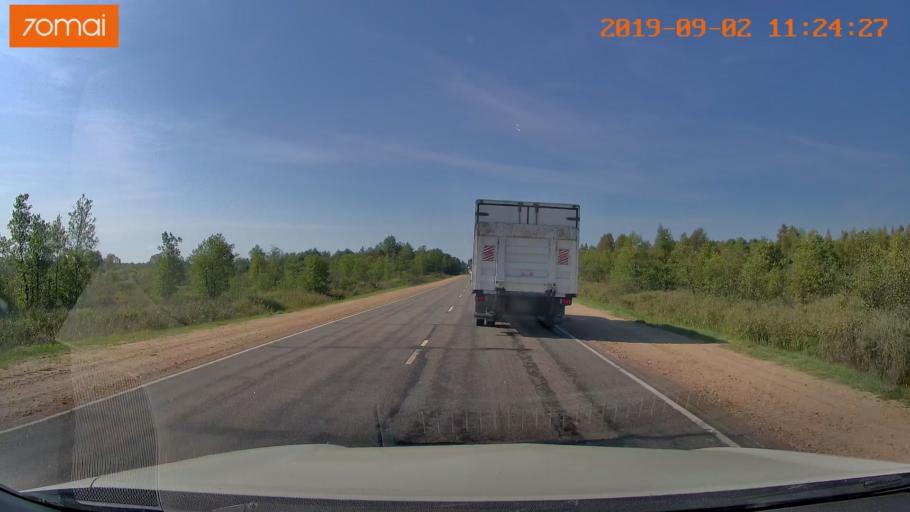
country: RU
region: Smolensk
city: Roslavl'
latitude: 54.0103
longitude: 32.9750
